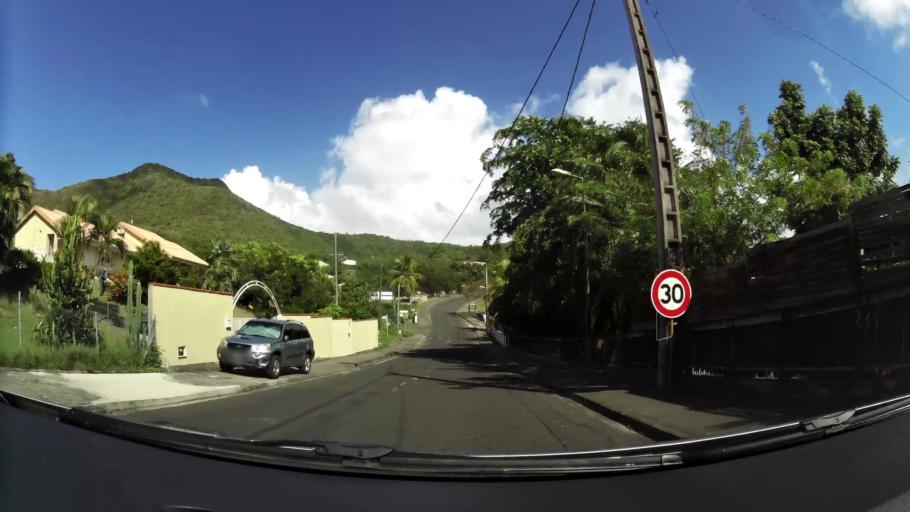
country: MQ
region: Martinique
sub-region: Martinique
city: Les Trois-Ilets
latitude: 14.4697
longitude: -61.0466
